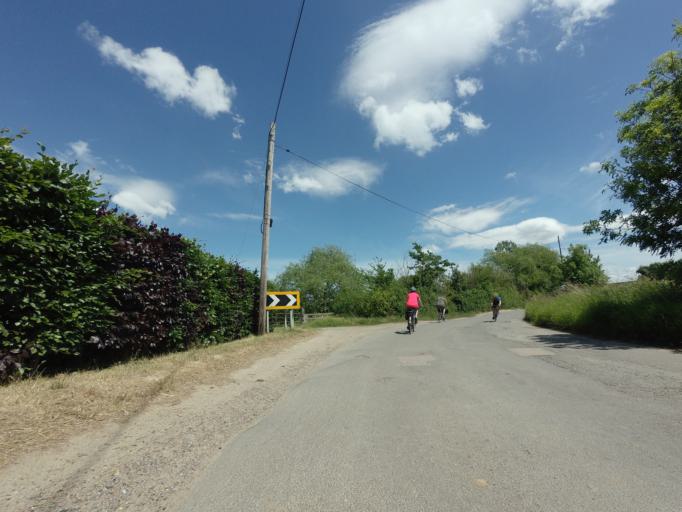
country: GB
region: England
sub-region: Medway
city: Cooling
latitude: 51.4571
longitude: 0.5329
